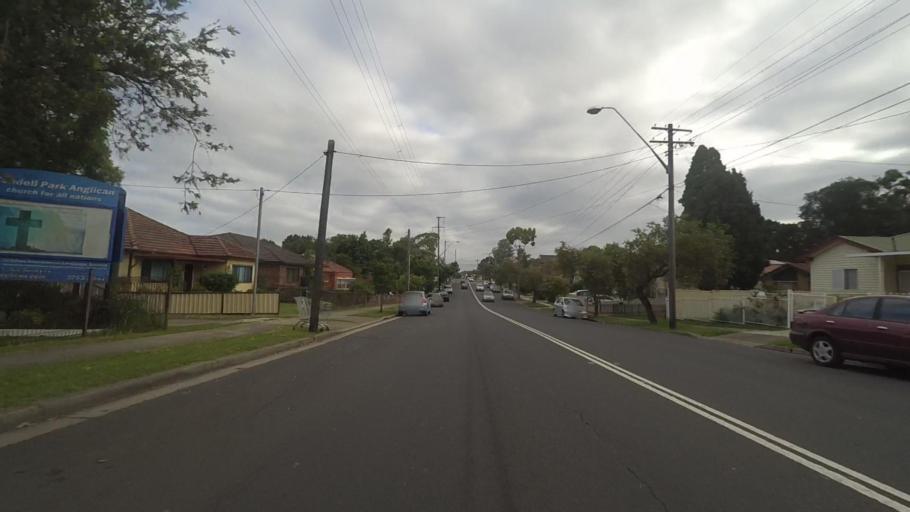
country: AU
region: New South Wales
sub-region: Bankstown
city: Bankstown
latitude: -33.9228
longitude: 151.0128
